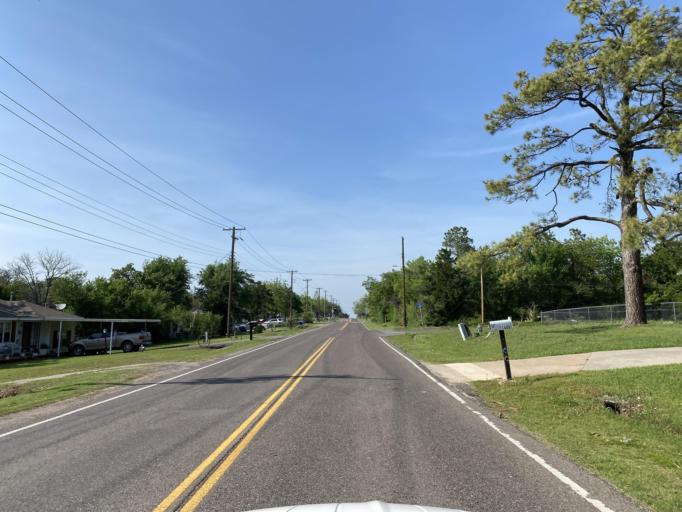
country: US
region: Oklahoma
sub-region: Oklahoma County
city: Nicoma Park
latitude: 35.4829
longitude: -97.3356
